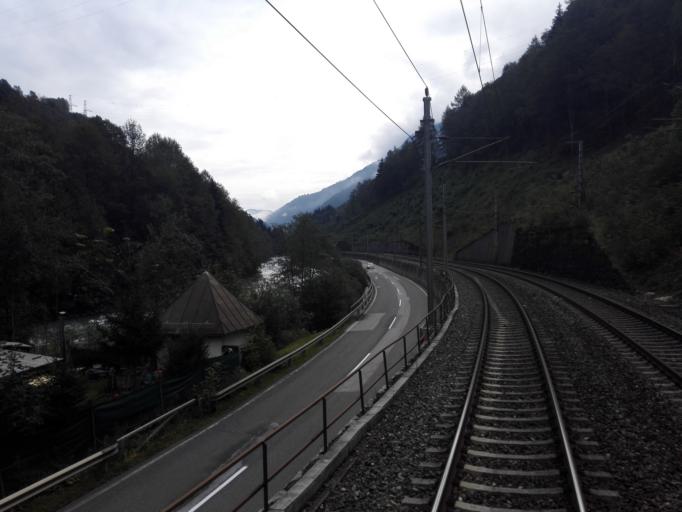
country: AT
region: Salzburg
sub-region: Politischer Bezirk Zell am See
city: Lend
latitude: 47.2985
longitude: 13.0766
